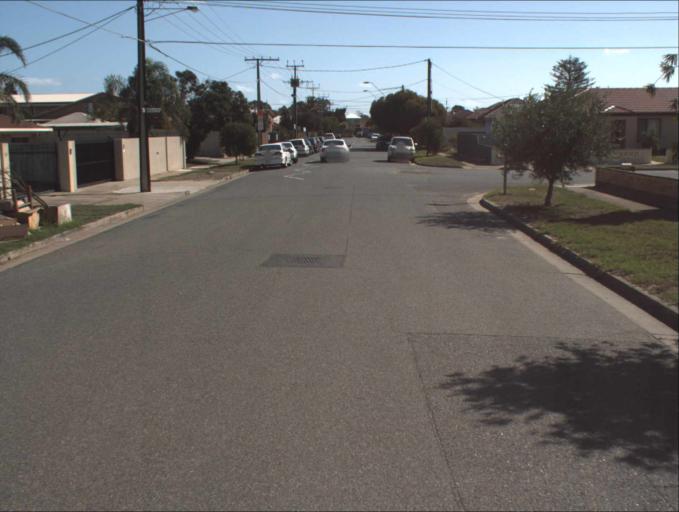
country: AU
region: South Australia
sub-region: Port Adelaide Enfield
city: Alberton
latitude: -34.8455
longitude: 138.5392
